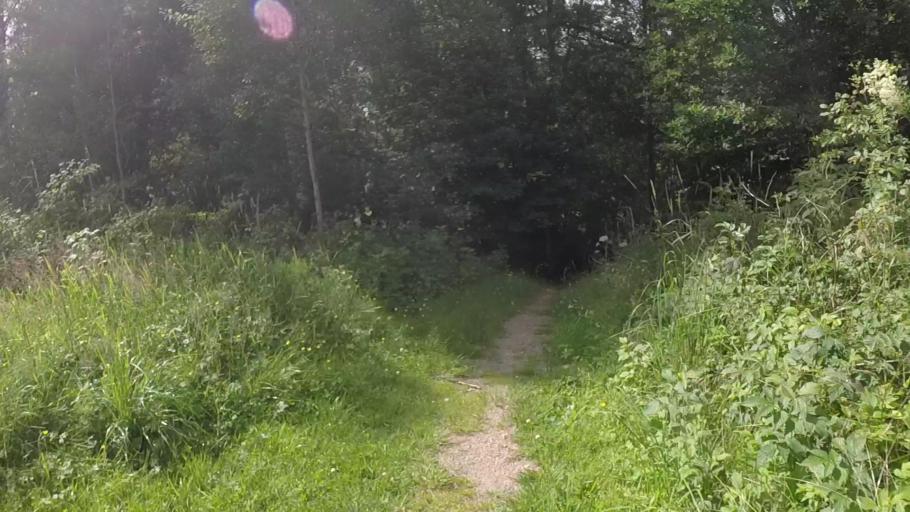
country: SE
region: Vaestra Goetaland
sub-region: Trollhattan
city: Trollhattan
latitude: 58.2536
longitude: 12.2671
